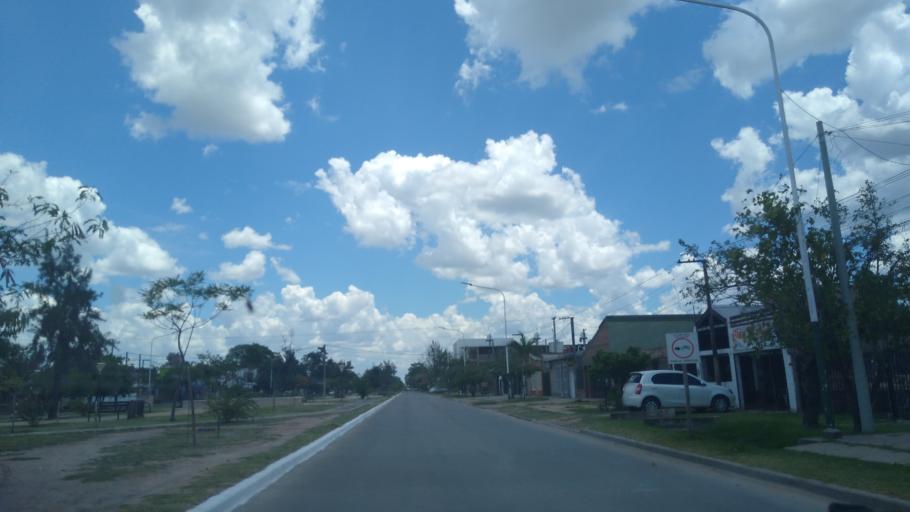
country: AR
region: Chaco
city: Presidencia Roque Saenz Pena
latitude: -26.7784
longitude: -60.4314
